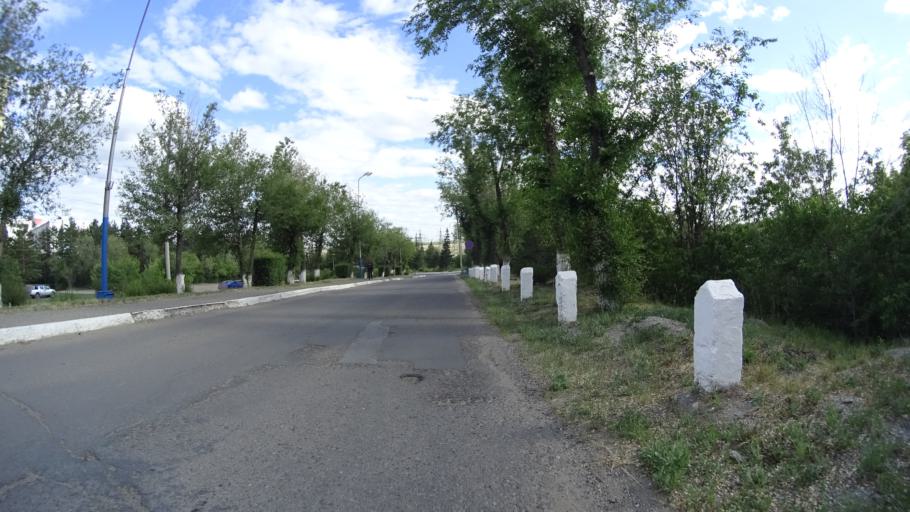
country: RU
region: Chelyabinsk
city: Troitsk
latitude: 54.0387
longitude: 61.6399
